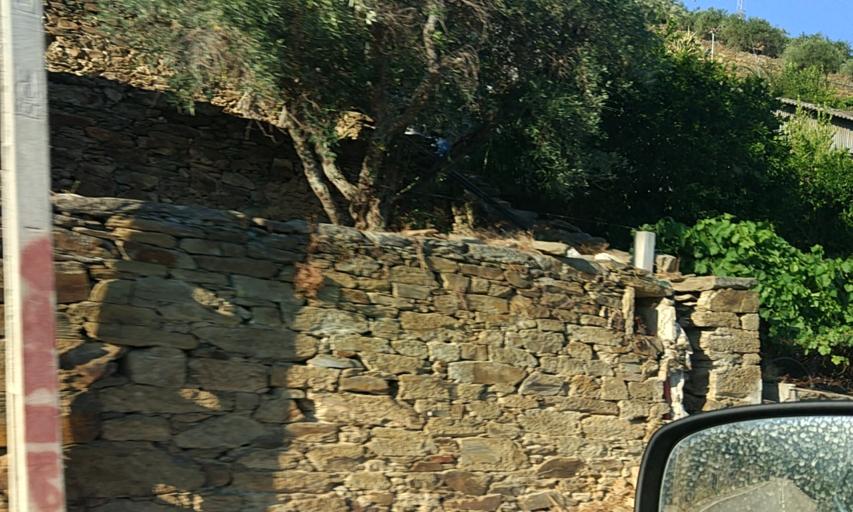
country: PT
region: Viseu
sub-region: Sao Joao da Pesqueira
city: Sao Joao da Pesqueira
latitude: 41.2111
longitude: -7.4267
